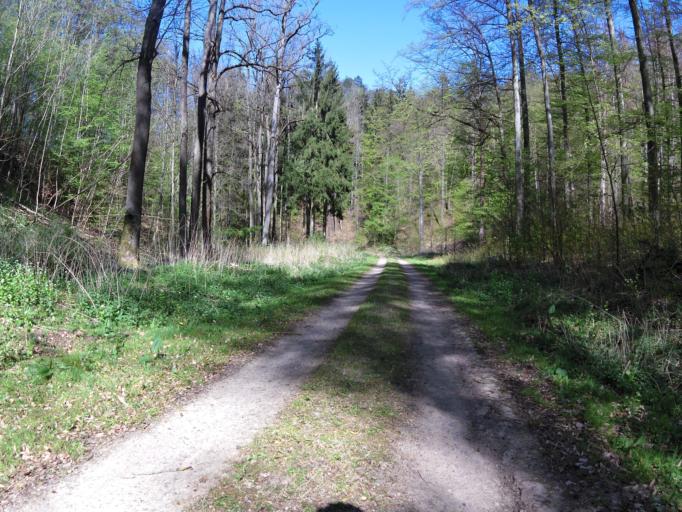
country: DE
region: Thuringia
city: Wolfsburg-Unkeroda
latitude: 50.9717
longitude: 10.2450
